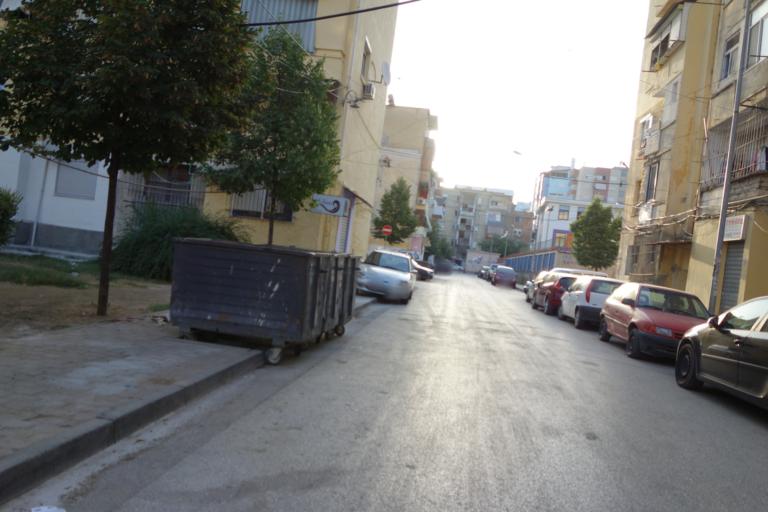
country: AL
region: Tirane
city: Tirana
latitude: 41.3229
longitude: 19.8056
